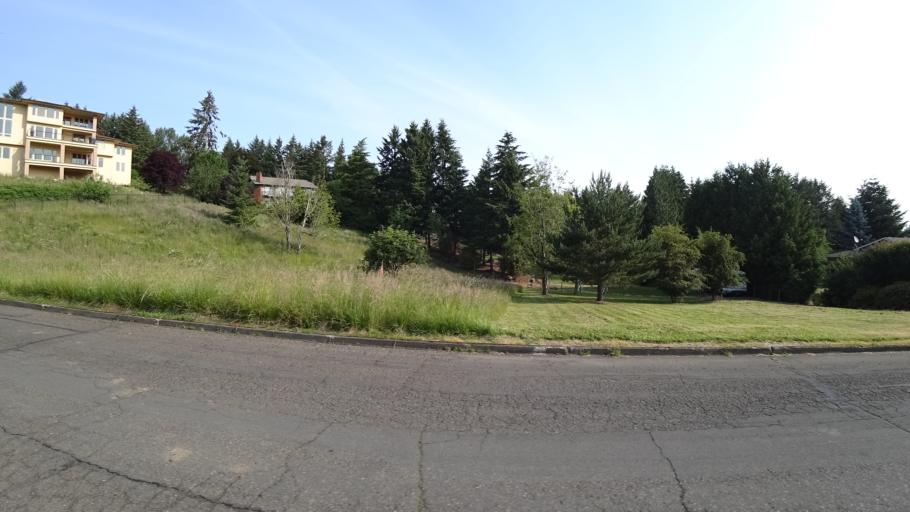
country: US
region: Oregon
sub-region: Clackamas County
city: Happy Valley
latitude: 45.4559
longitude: -122.5329
